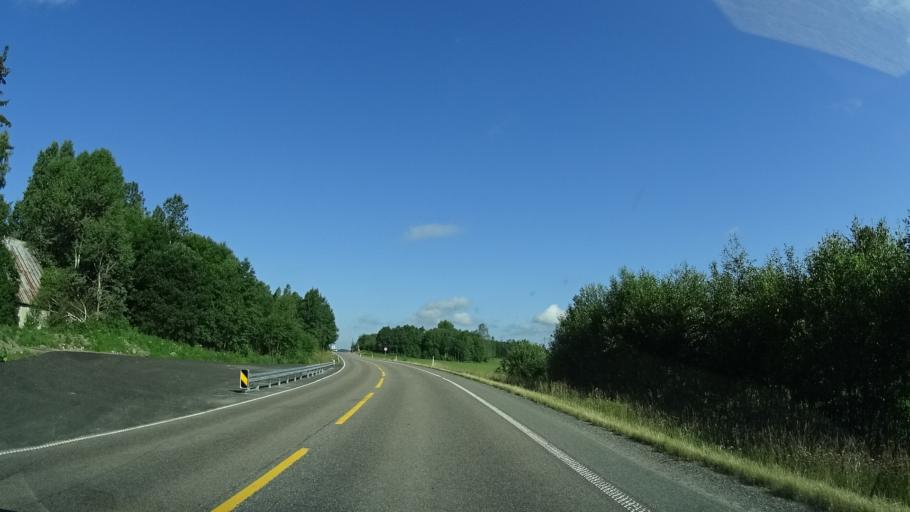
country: NO
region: Ostfold
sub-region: Hobol
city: Elvestad
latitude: 59.6652
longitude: 10.9053
